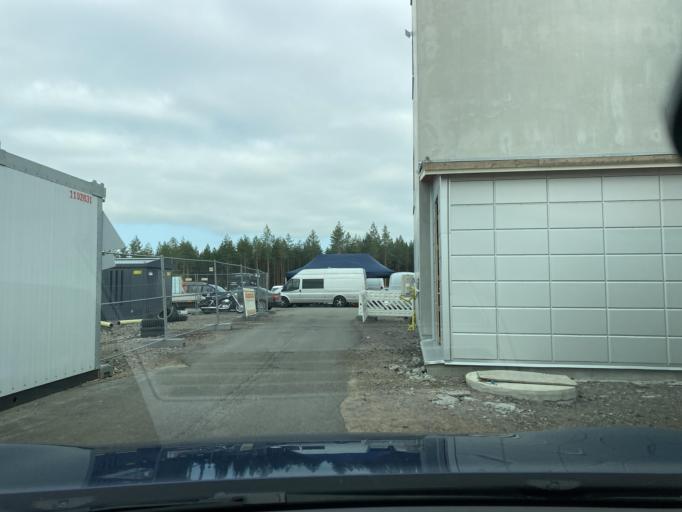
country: FI
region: Kymenlaakso
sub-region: Kouvola
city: Iitti
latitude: 60.8828
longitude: 26.4837
